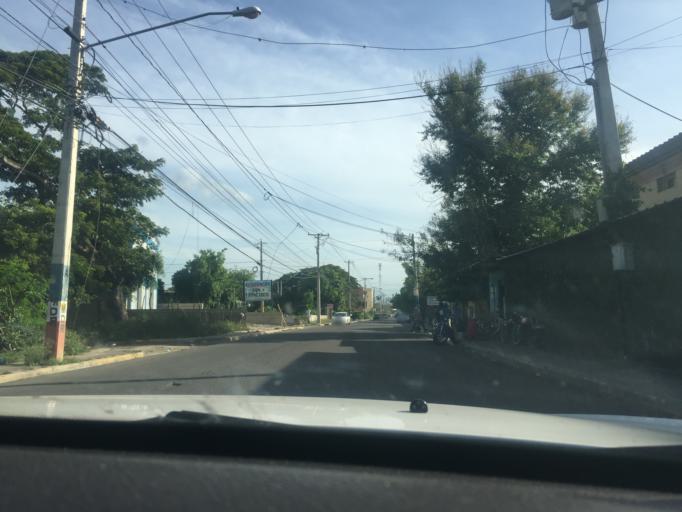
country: DO
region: Santiago
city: Tamboril
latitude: 19.4745
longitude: -70.6434
